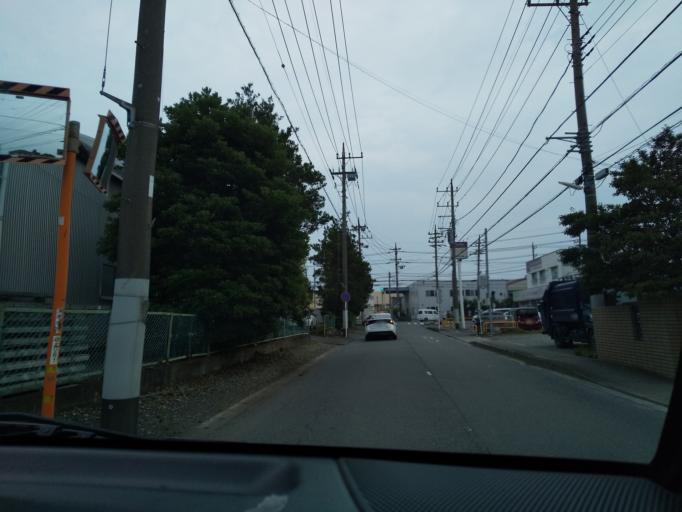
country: JP
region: Kanagawa
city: Atsugi
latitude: 35.4071
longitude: 139.3891
